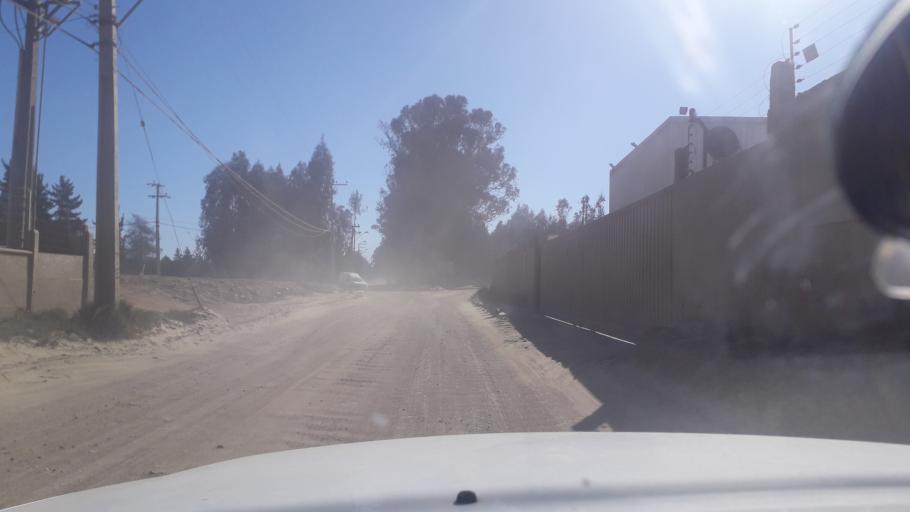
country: CL
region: Valparaiso
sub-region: Provincia de Valparaiso
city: Vina del Mar
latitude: -32.9590
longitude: -71.5123
